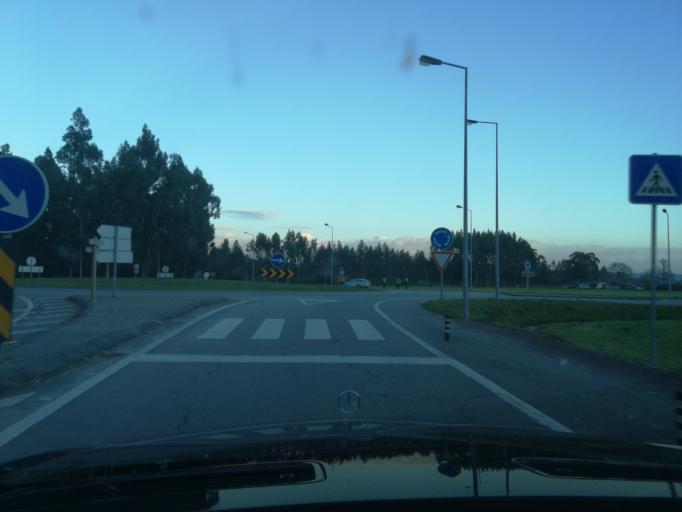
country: PT
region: Aveiro
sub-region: Estarreja
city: Estarreja
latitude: 40.7580
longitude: -8.5964
